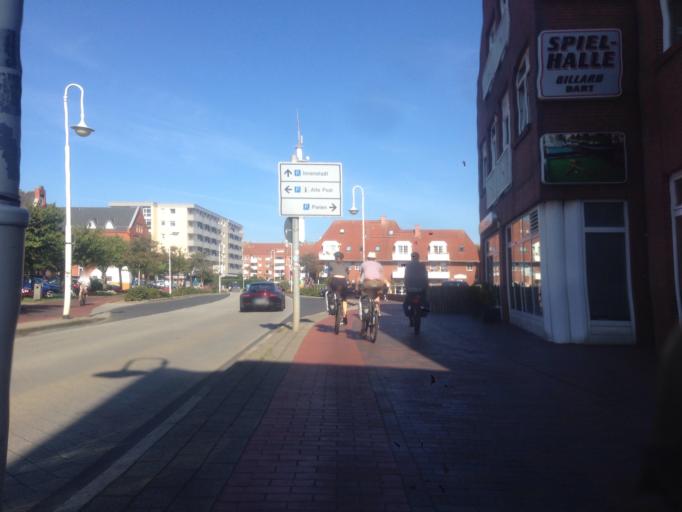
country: DE
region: Schleswig-Holstein
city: Westerland
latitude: 54.9080
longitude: 8.3087
